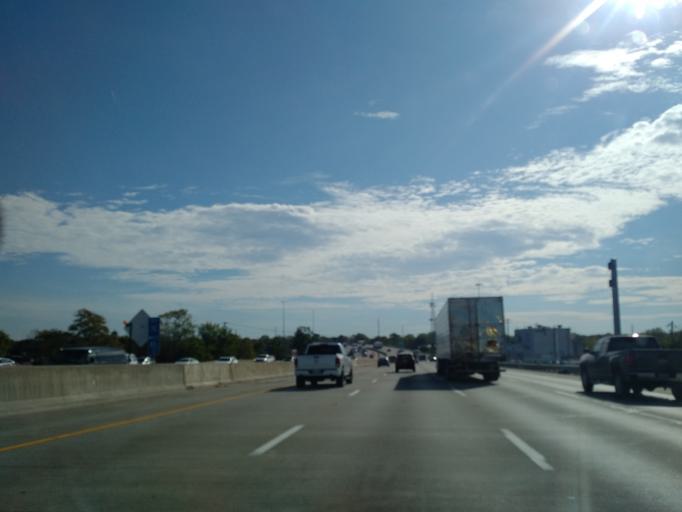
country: US
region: Indiana
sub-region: Marion County
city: Indianapolis
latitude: 39.7979
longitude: -86.1085
